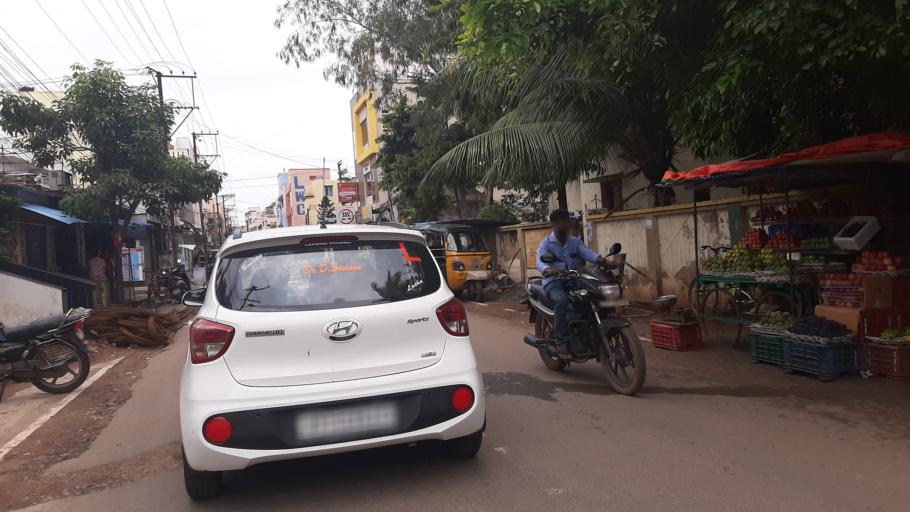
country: IN
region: Andhra Pradesh
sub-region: Vishakhapatnam
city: Yarada
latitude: 17.7234
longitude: 83.3326
